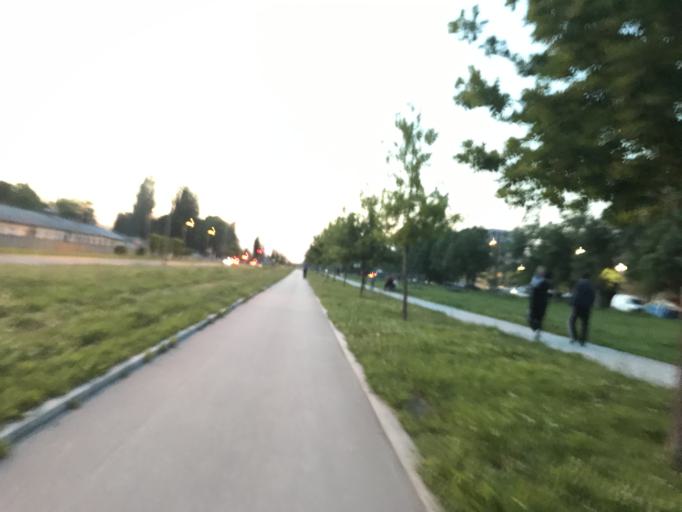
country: RS
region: Autonomna Pokrajina Vojvodina
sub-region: Juznobacki Okrug
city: Novi Sad
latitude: 45.2645
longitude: 19.8060
